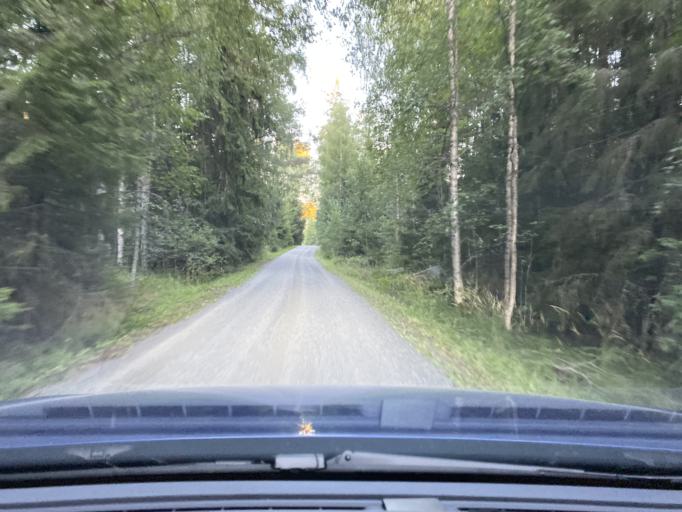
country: FI
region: Satakunta
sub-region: Rauma
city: Kiukainen
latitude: 61.1323
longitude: 22.0247
